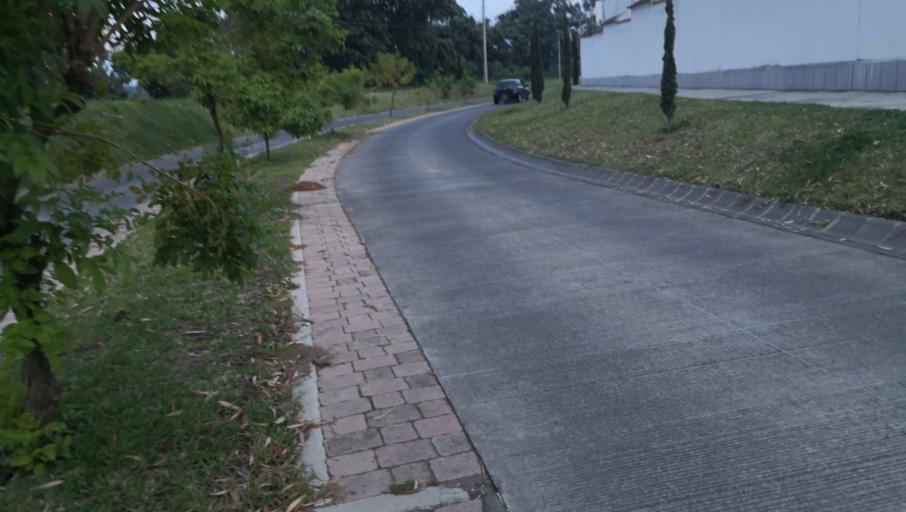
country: GT
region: Guatemala
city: Villa Nueva
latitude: 14.5622
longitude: -90.5962
